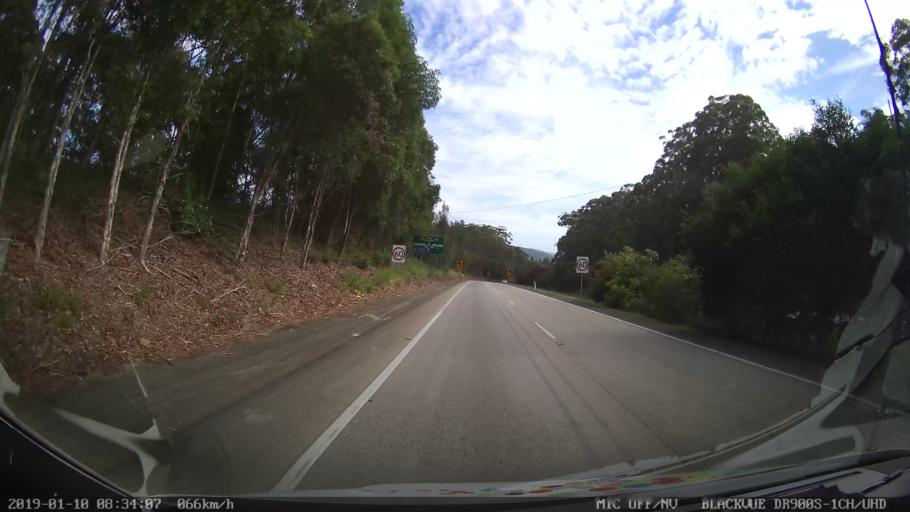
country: AU
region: New South Wales
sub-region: Coffs Harbour
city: Boambee
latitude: -30.3241
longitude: 153.0837
